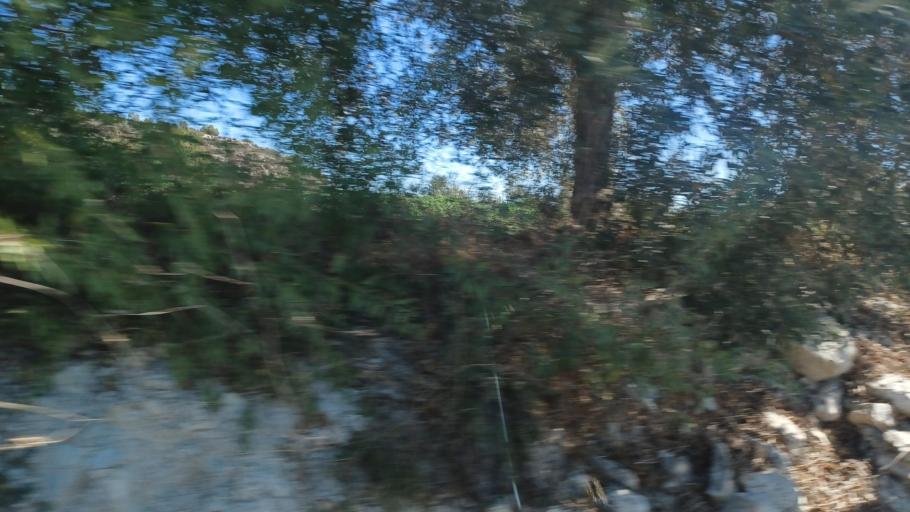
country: CY
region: Pafos
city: Mesogi
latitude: 34.8305
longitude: 32.4788
